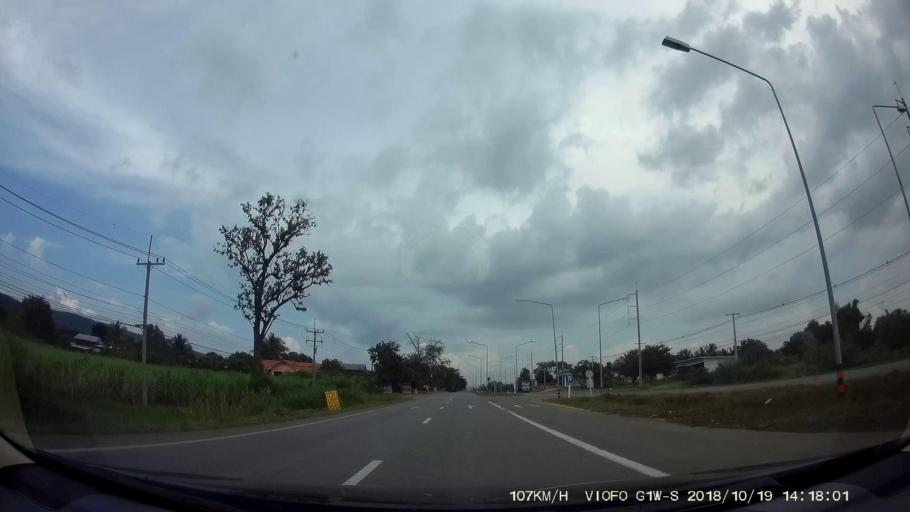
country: TH
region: Chaiyaphum
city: Khon Sawan
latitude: 16.0107
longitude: 102.2310
